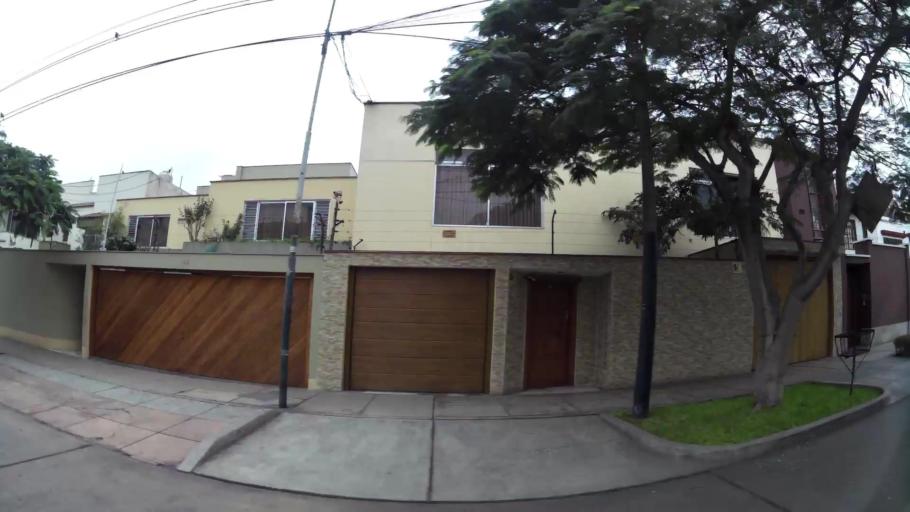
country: PE
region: Lima
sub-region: Lima
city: San Luis
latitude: -12.0964
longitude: -77.0153
